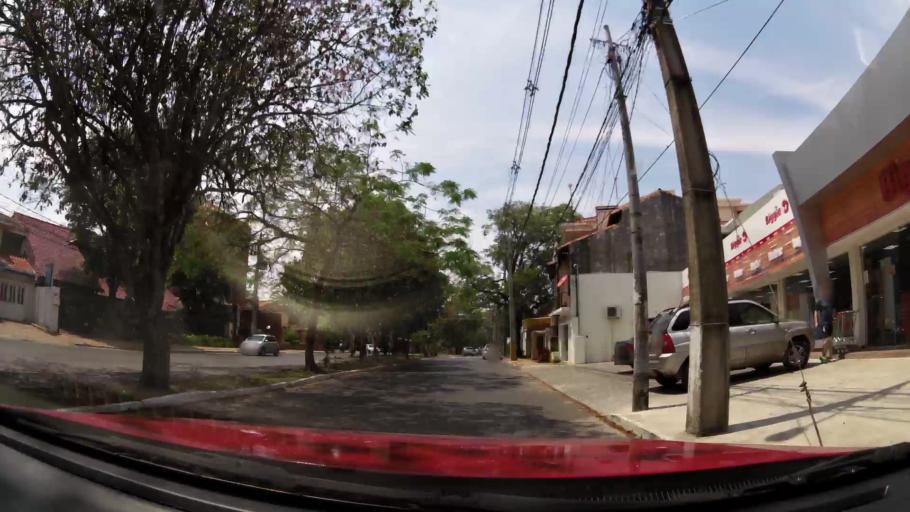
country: PY
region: Central
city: Lambare
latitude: -25.2990
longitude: -57.5734
